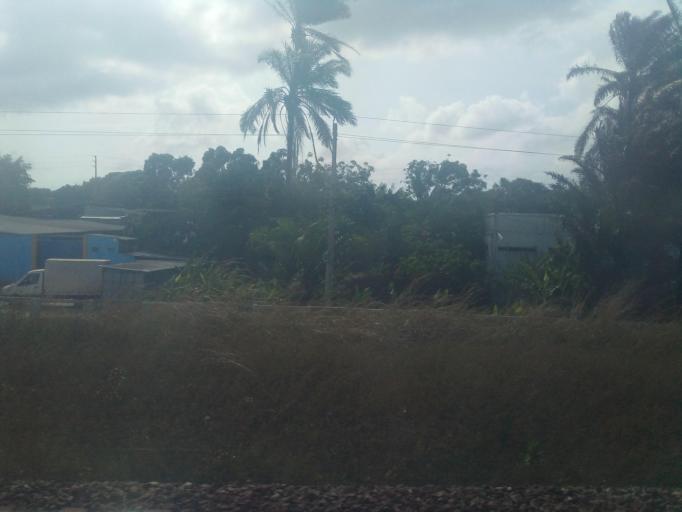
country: BR
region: Maranhao
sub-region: Sao Luis
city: Sao Luis
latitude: -2.6911
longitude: -44.3034
